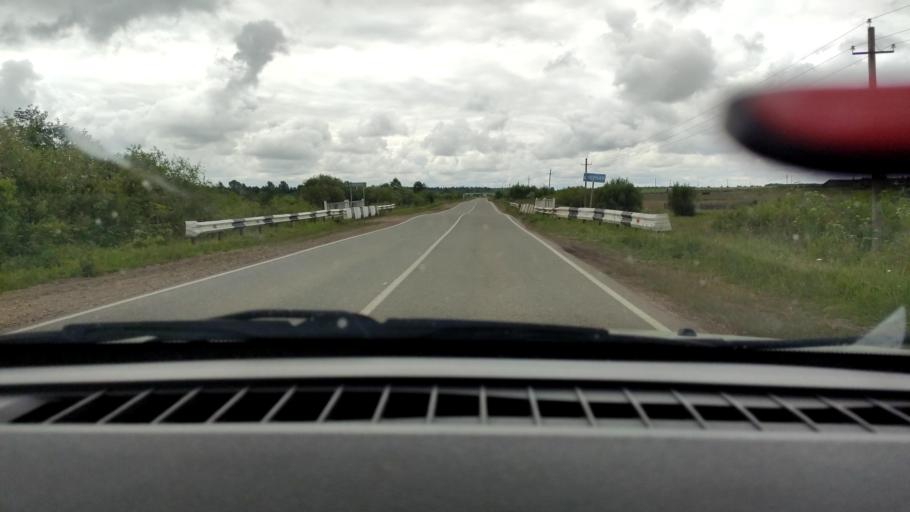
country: RU
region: Perm
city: Chaykovskaya
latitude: 58.0829
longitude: 55.6154
